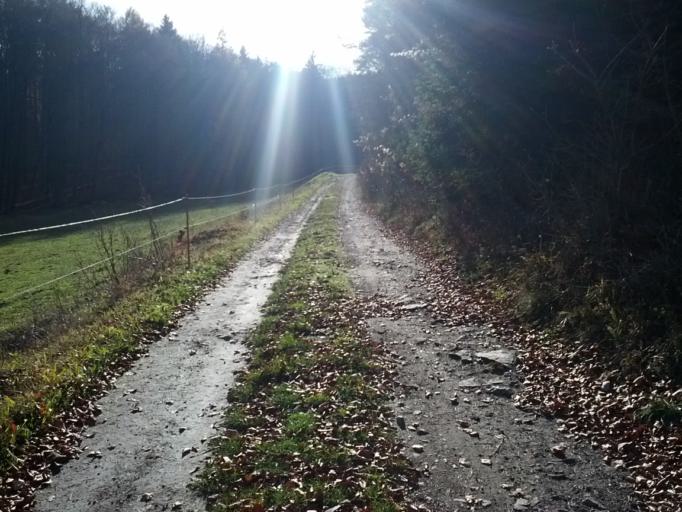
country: DE
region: Thuringia
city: Eisenach
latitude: 50.9522
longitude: 10.3525
